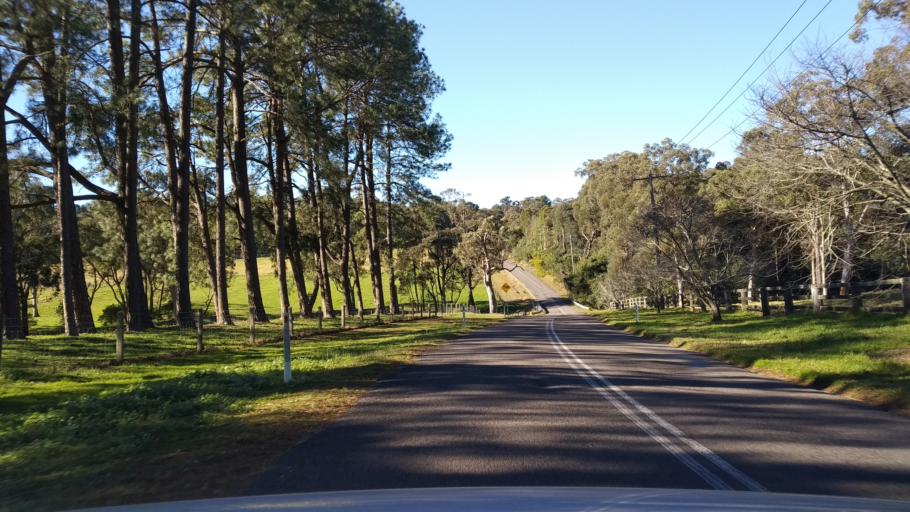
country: AU
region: New South Wales
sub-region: Wyong Shire
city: Little Jilliby
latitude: -33.2359
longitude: 151.2388
